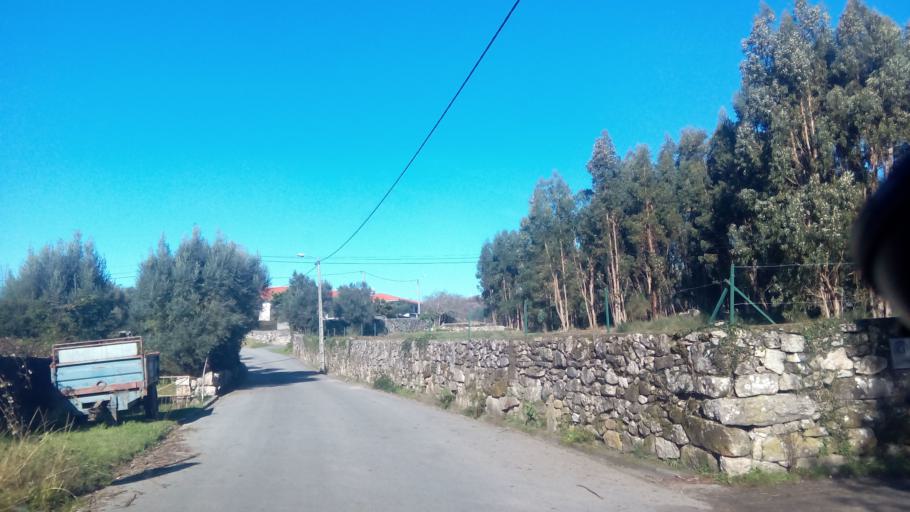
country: PT
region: Viana do Castelo
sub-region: Viana do Castelo
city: Darque
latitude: 41.7425
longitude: -8.7357
